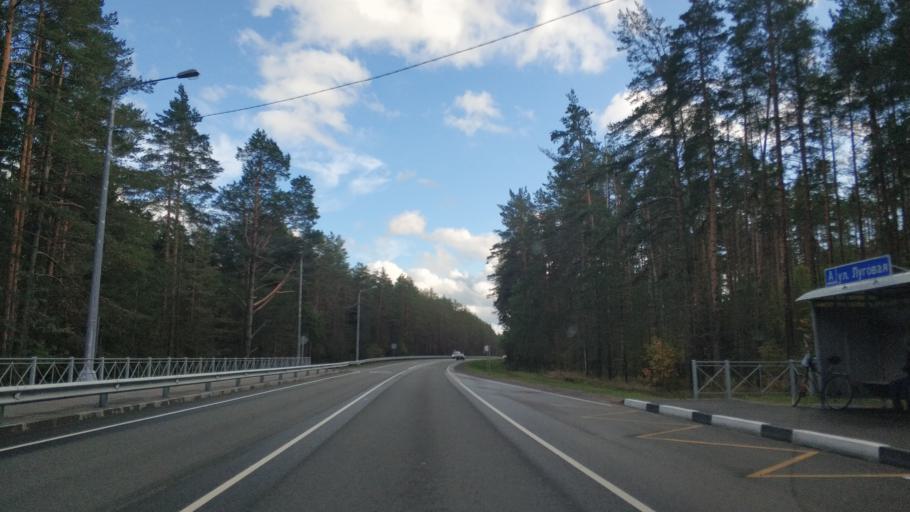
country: RU
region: Leningrad
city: Priozersk
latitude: 60.9939
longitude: 30.1828
